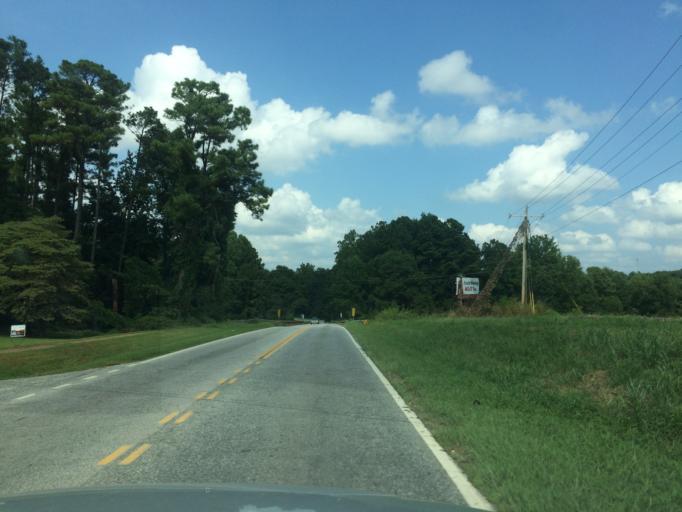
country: US
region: South Carolina
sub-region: Spartanburg County
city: Fairforest
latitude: 34.9600
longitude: -82.0057
